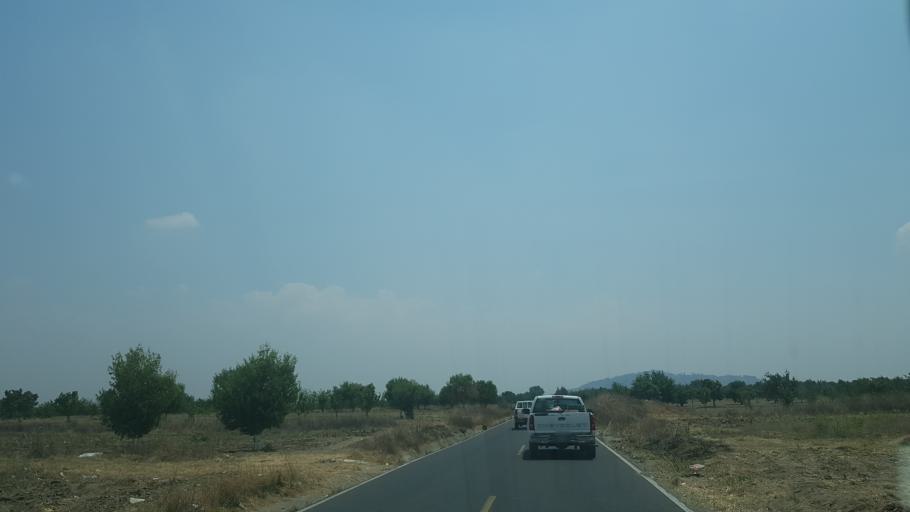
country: MX
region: Puebla
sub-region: San Jeronimo Tecuanipan
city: San Miguel Papaxtla
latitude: 19.0942
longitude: -98.4014
